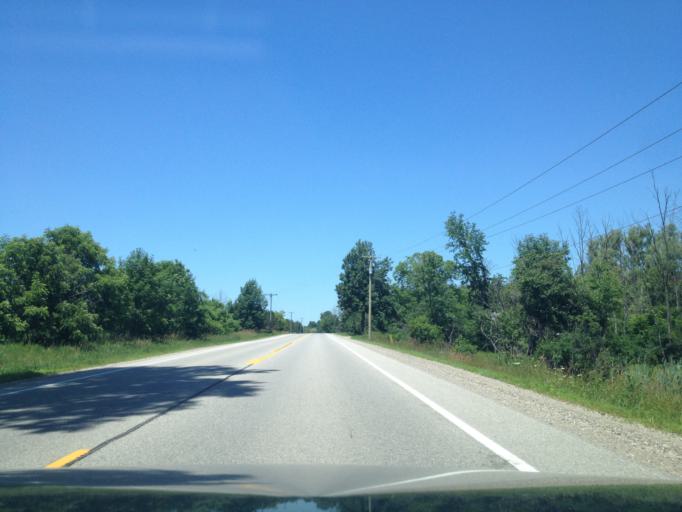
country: CA
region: Ontario
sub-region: Wellington County
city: Guelph
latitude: 43.6045
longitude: -80.1981
